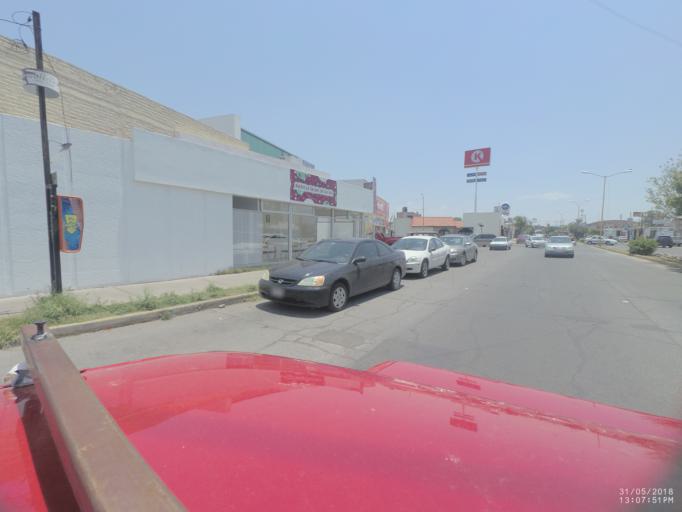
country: MX
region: Aguascalientes
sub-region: Aguascalientes
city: Aguascalientes
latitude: 21.8728
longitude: -102.2907
